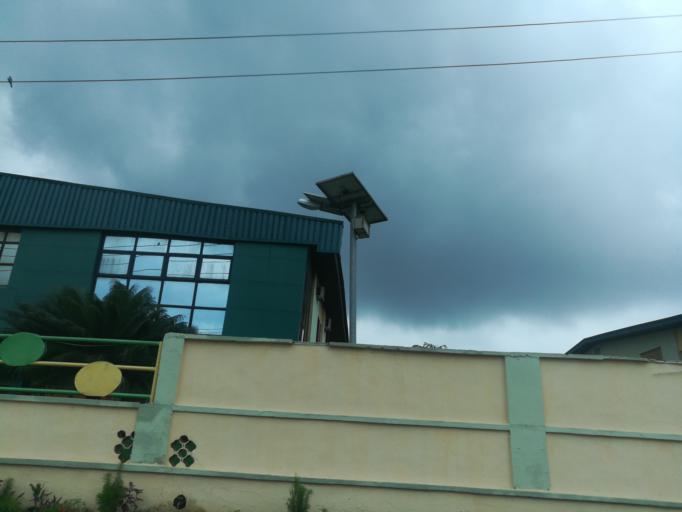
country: NG
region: Lagos
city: Agege
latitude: 6.6156
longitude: 3.3399
